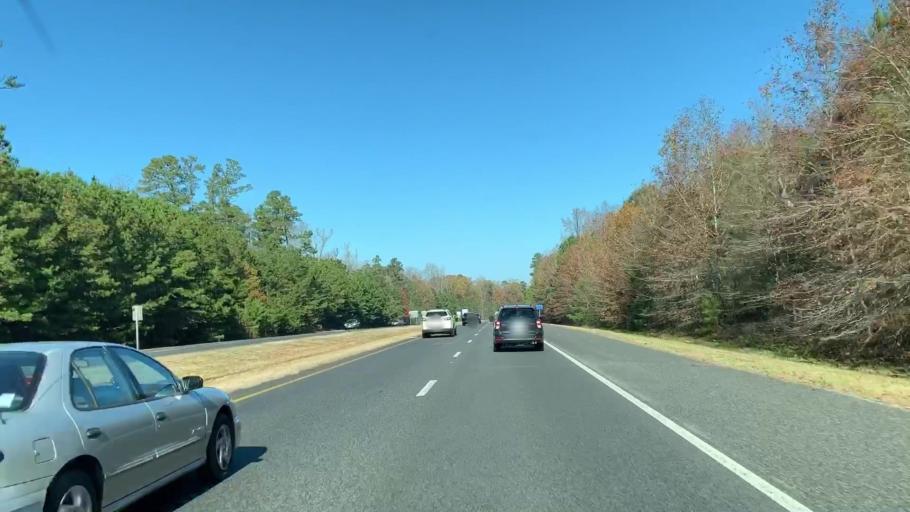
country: US
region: Virginia
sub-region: James City County
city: Williamsburg
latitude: 37.3121
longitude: -76.7477
